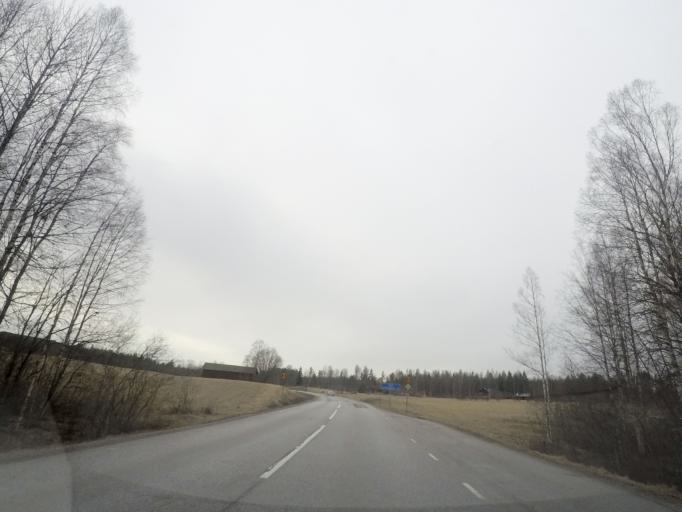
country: SE
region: Vaestmanland
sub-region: Skinnskattebergs Kommun
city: Skinnskatteberg
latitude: 59.8732
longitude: 15.6475
